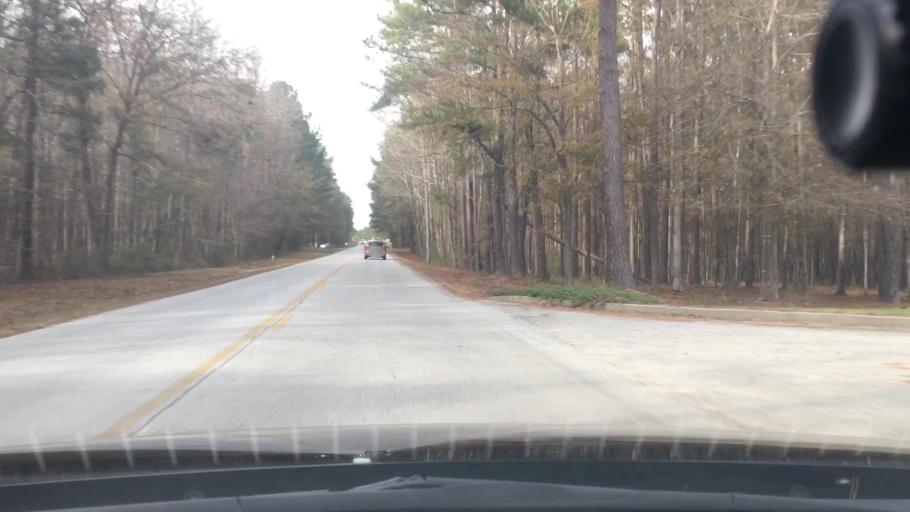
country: US
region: Georgia
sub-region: Coweta County
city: Senoia
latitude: 33.3061
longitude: -84.4676
